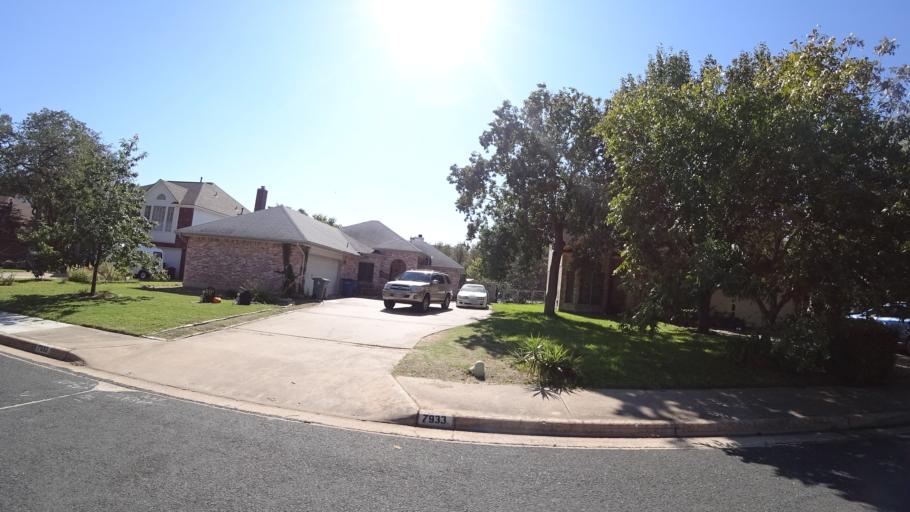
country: US
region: Texas
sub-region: Travis County
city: Shady Hollow
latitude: 30.2187
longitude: -97.8686
